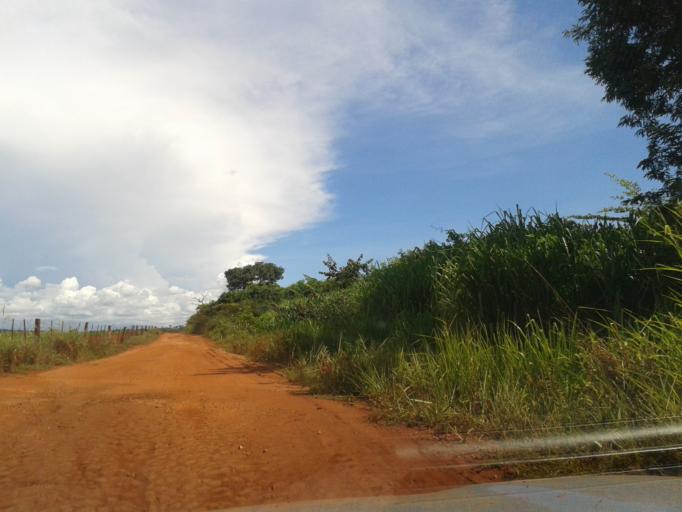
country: BR
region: Minas Gerais
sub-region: Capinopolis
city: Capinopolis
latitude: -18.7091
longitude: -49.7723
